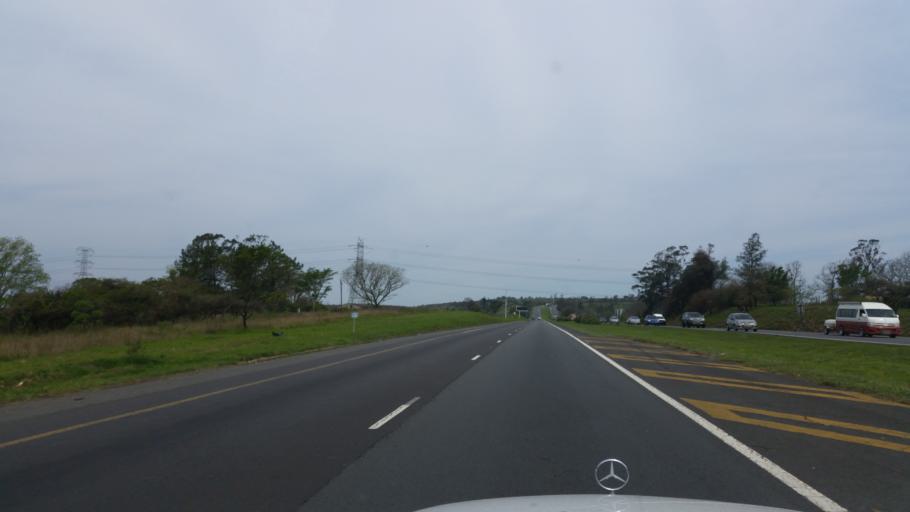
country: ZA
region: KwaZulu-Natal
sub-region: uMgungundlovu District Municipality
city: Camperdown
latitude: -29.6965
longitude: 30.4867
